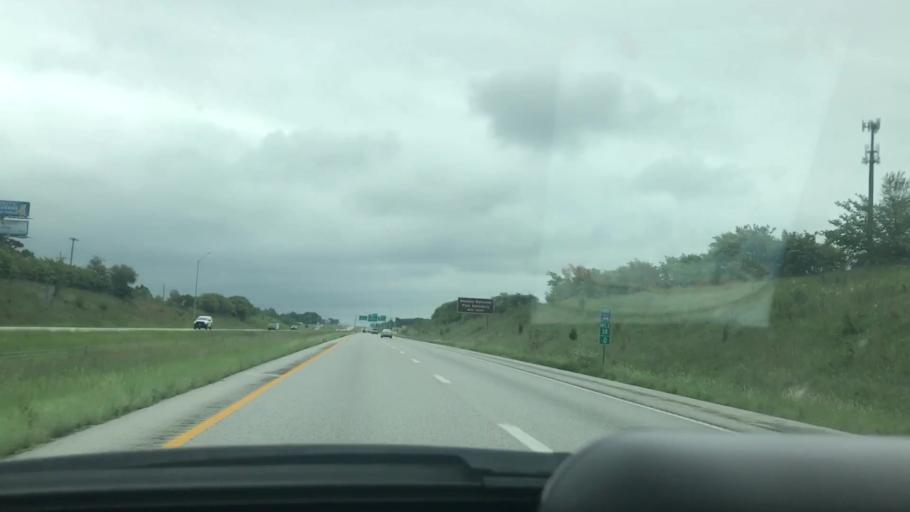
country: US
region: Missouri
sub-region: Jasper County
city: Duenweg
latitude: 37.0818
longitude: -94.3215
